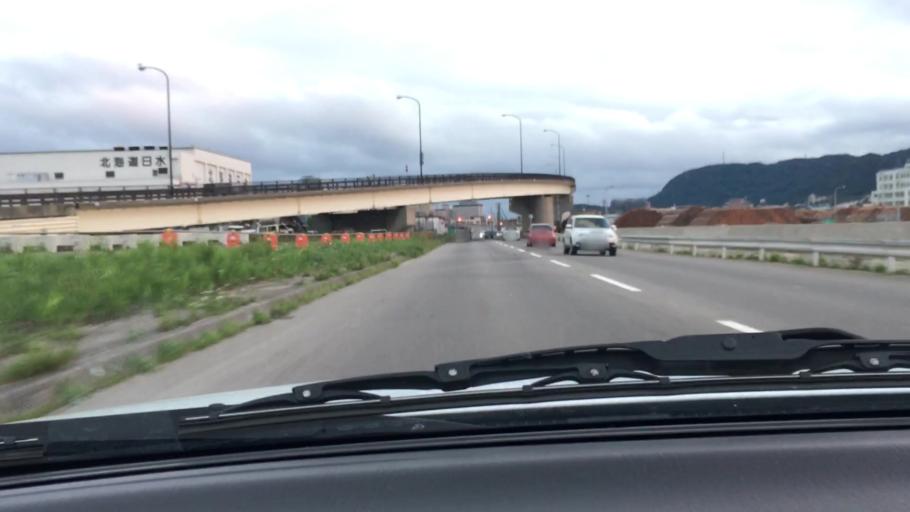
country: JP
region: Hokkaido
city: Hakodate
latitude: 41.7860
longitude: 140.7272
